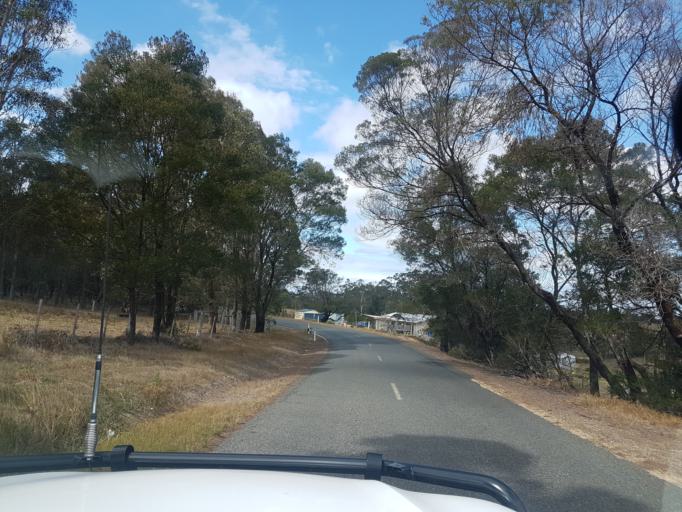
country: AU
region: Victoria
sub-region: East Gippsland
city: Bairnsdale
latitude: -37.7893
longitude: 147.5829
